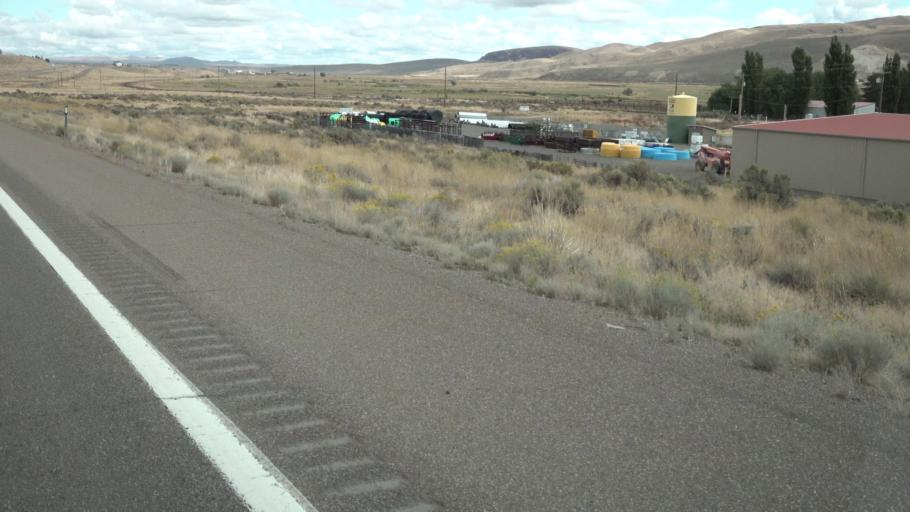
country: US
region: Nevada
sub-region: Elko County
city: Elko
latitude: 40.9125
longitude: -115.6935
